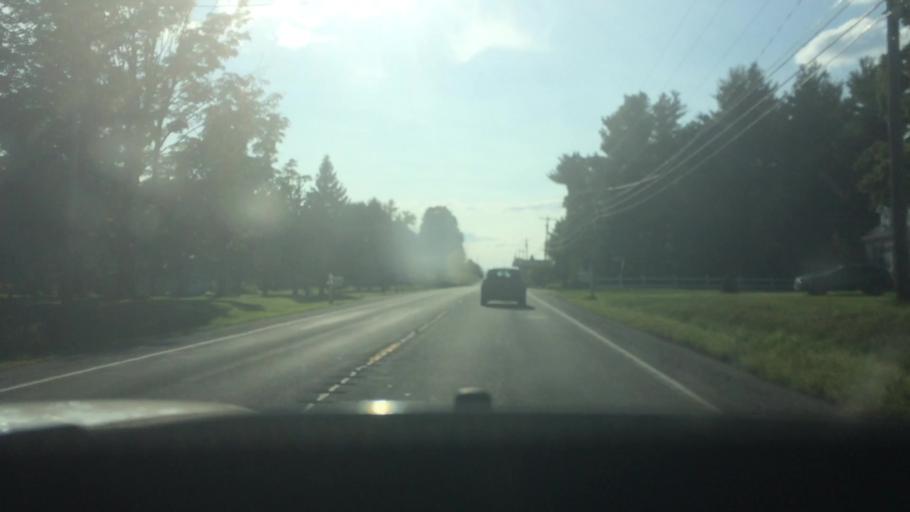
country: US
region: New York
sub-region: St. Lawrence County
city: Potsdam
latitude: 44.6701
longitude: -74.9316
